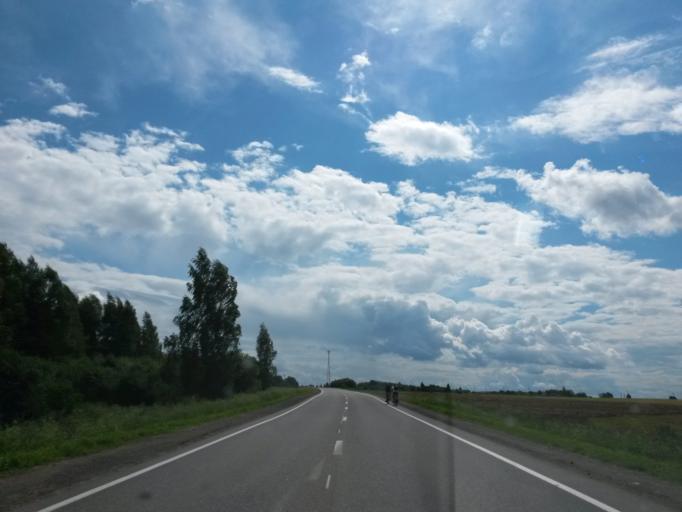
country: RU
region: Jaroslavl
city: Gavrilov-Yam
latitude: 57.3159
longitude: 39.9335
